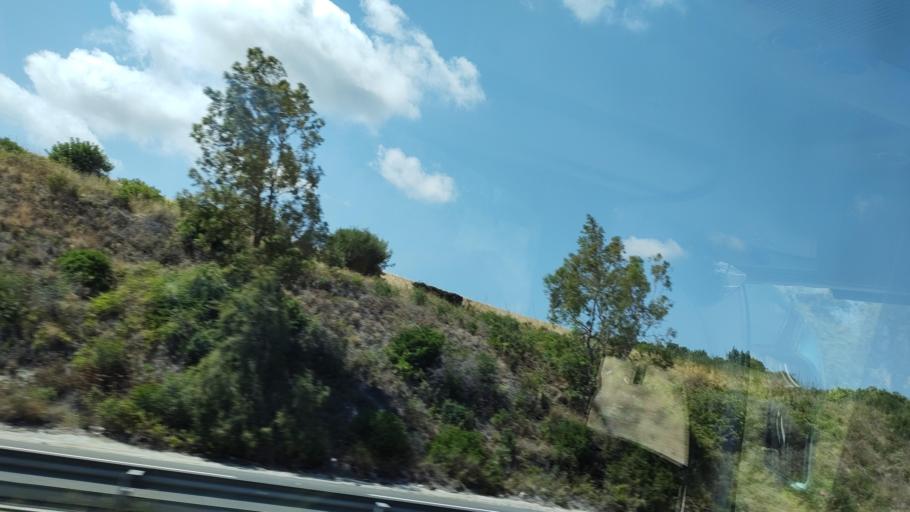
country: ES
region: Andalusia
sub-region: Provincia de Malaga
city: Manilva
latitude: 36.3926
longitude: -5.2530
